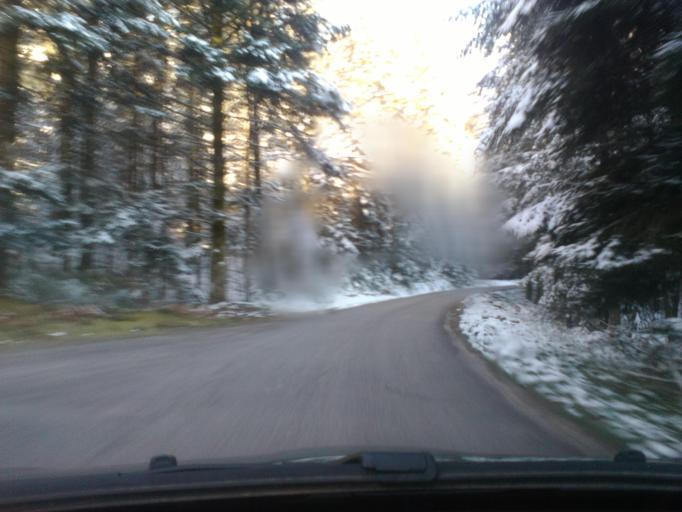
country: FR
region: Lorraine
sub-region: Departement des Vosges
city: Taintrux
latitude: 48.2200
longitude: 6.8706
